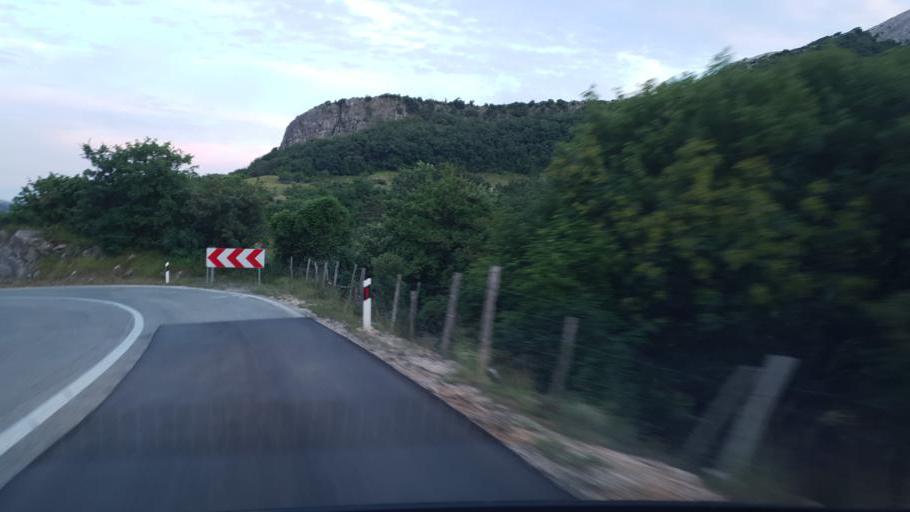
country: HR
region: Primorsko-Goranska
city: Punat
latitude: 45.0203
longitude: 14.6856
